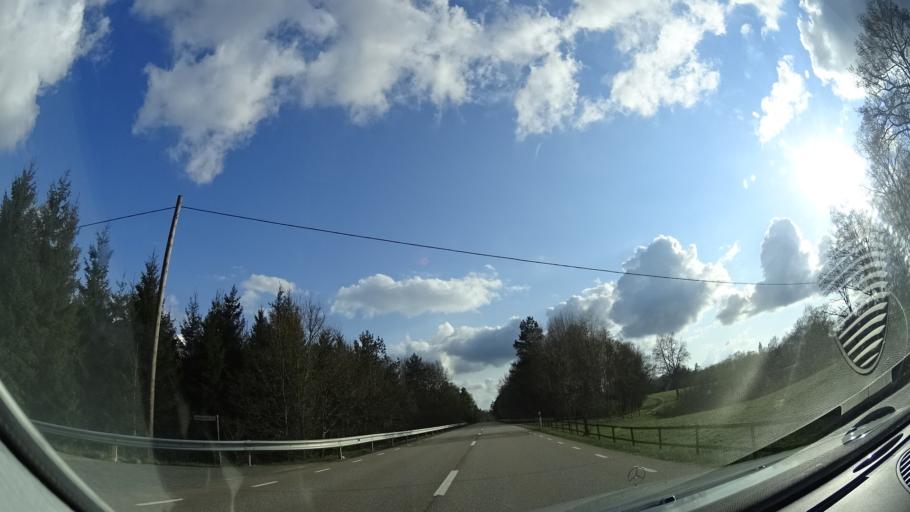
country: SE
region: Skane
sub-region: Perstorps Kommun
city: Perstorp
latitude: 56.1238
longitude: 13.3028
